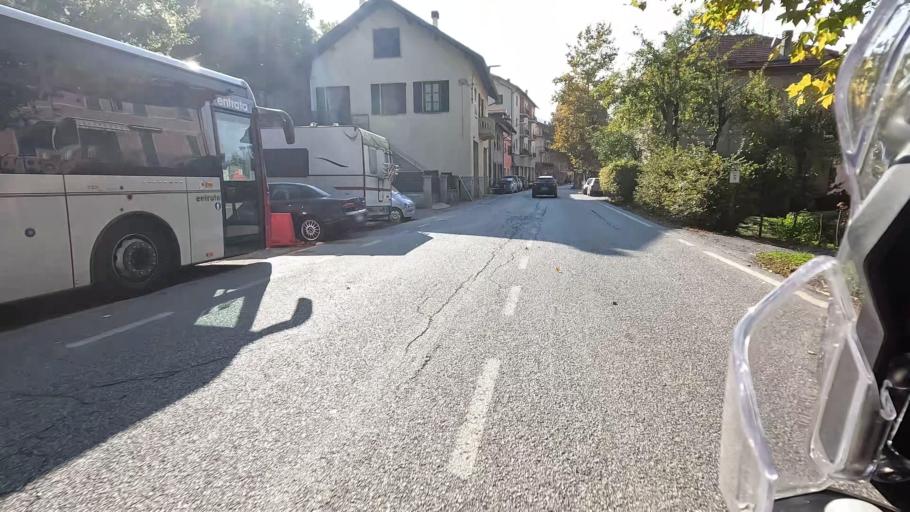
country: IT
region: Liguria
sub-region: Provincia di Savona
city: Sassello
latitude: 44.4799
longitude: 8.4927
